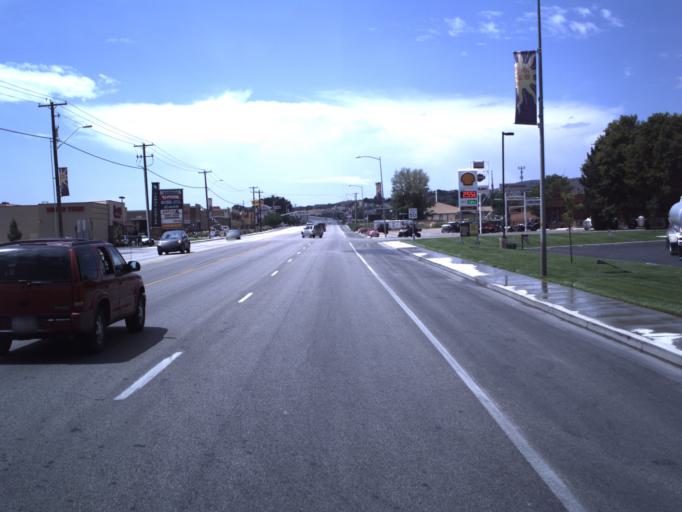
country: US
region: Utah
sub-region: Uintah County
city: Vernal
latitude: 40.4390
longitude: -109.5656
